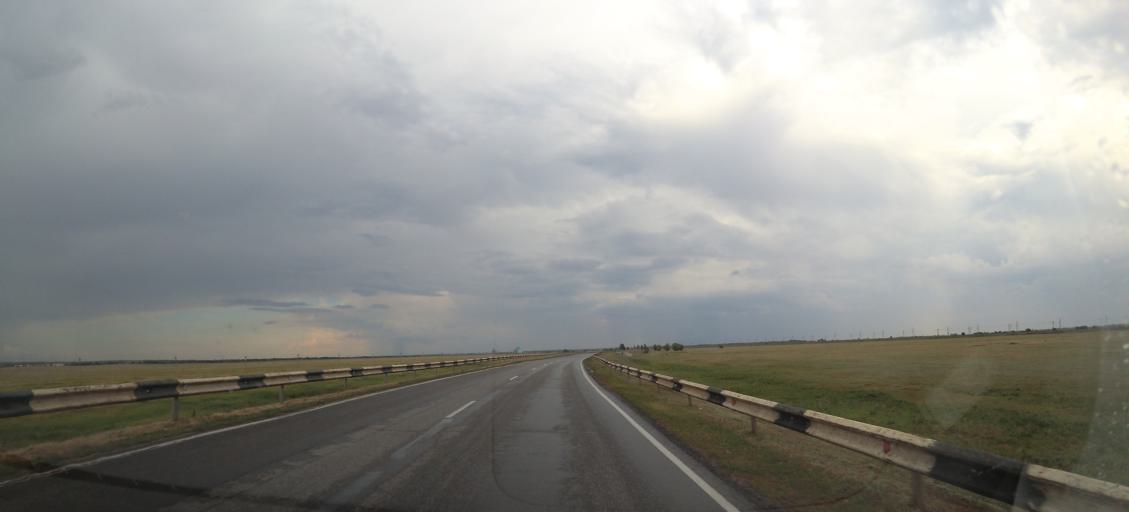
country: RU
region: Rostov
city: Dubovskoye
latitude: 47.3825
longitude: 42.6928
